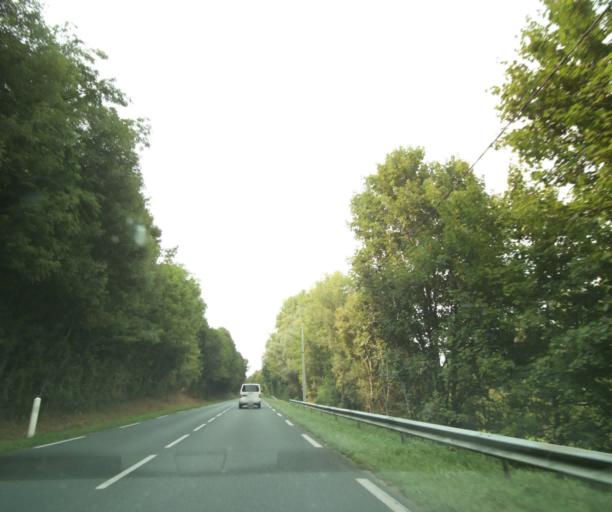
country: FR
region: Centre
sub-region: Departement de l'Indre
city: Clion
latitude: 46.9634
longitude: 1.2064
